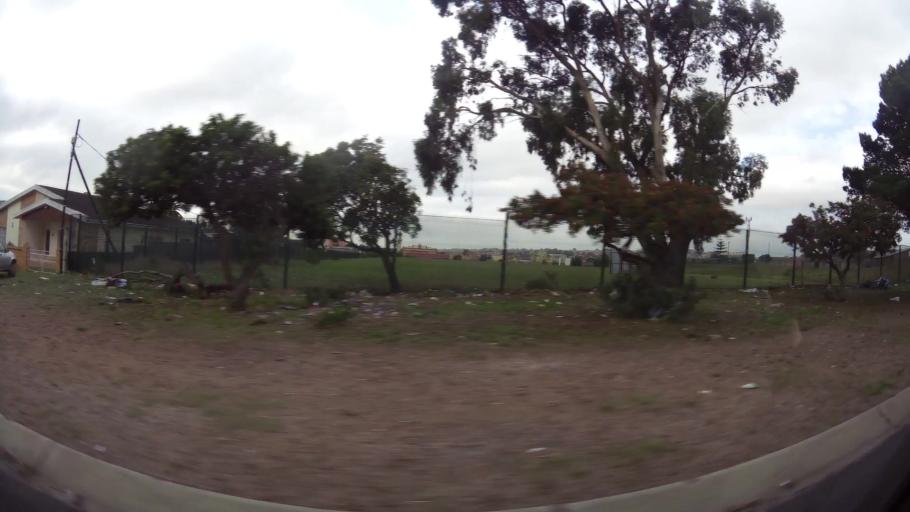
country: ZA
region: Eastern Cape
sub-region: Nelson Mandela Bay Metropolitan Municipality
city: Port Elizabeth
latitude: -33.9175
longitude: 25.5587
